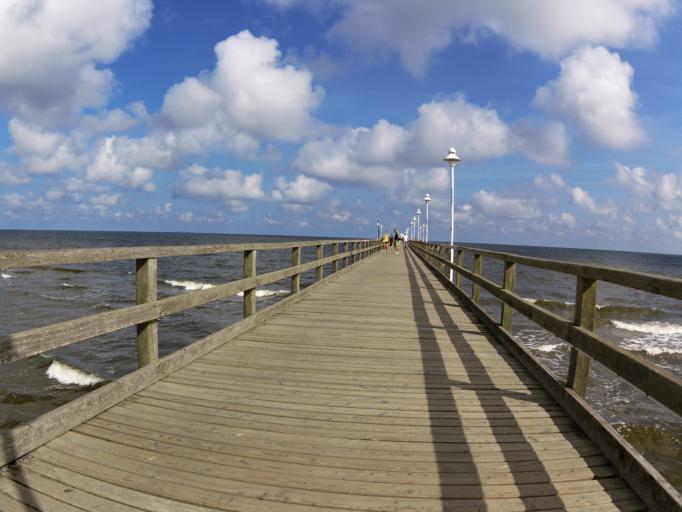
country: DE
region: Mecklenburg-Vorpommern
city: Ostseebad Zinnowitz
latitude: 54.0822
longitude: 13.9157
